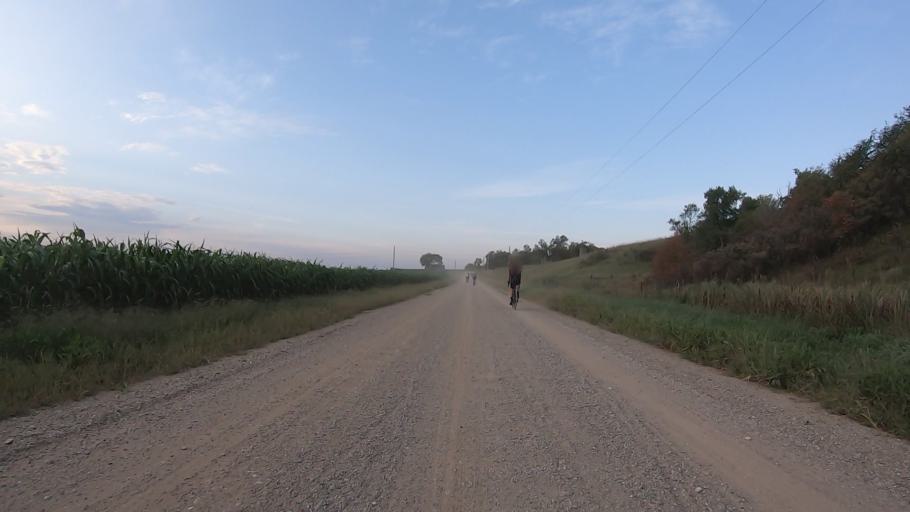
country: US
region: Kansas
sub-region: Marshall County
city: Marysville
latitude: 39.8239
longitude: -96.6662
